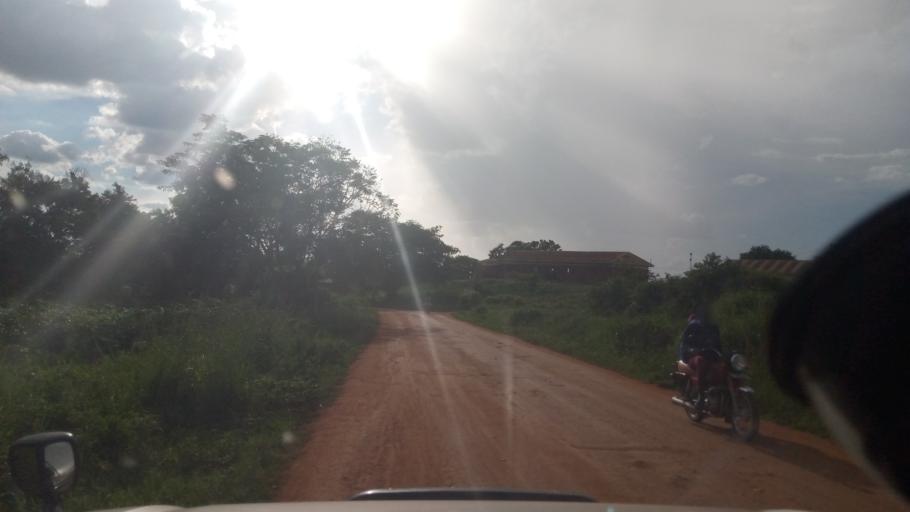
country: UG
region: Northern Region
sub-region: Lira District
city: Lira
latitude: 2.2285
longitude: 32.9013
